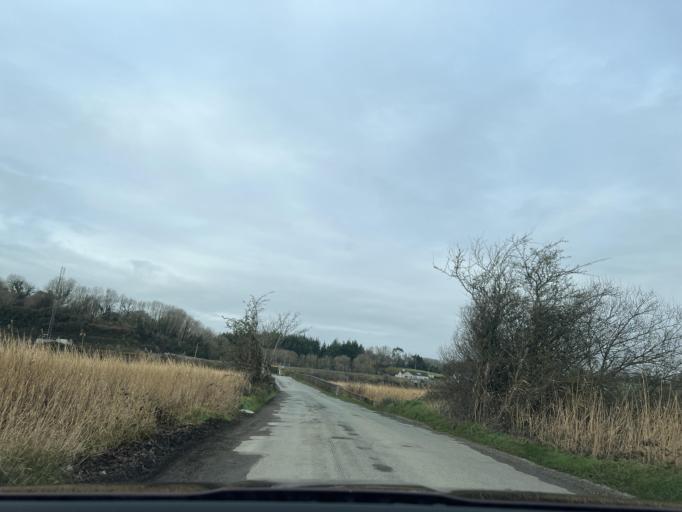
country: IE
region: Leinster
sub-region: Loch Garman
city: Castlebridge
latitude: 52.3847
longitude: -6.5658
